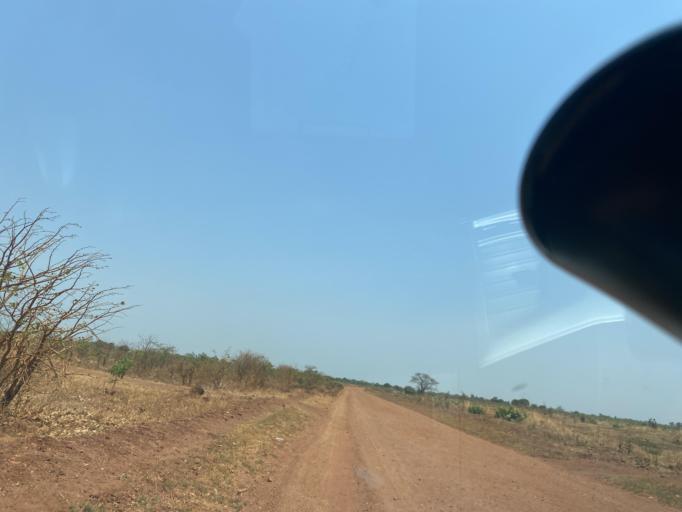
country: ZM
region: Southern
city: Nakambala
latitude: -15.5034
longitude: 27.9217
